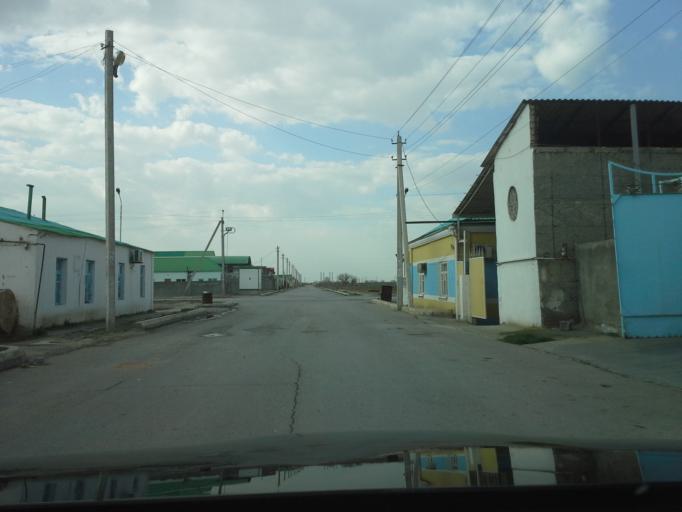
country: TM
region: Ahal
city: Ashgabat
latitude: 37.9921
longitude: 58.2916
